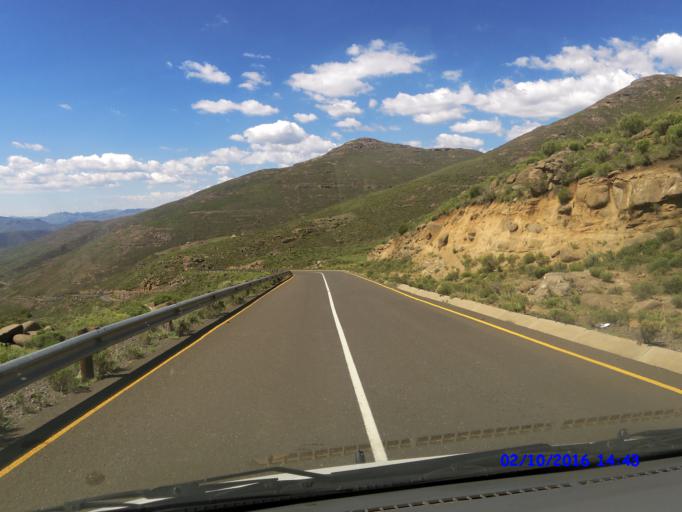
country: LS
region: Maseru
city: Nako
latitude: -29.5290
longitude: 28.0592
